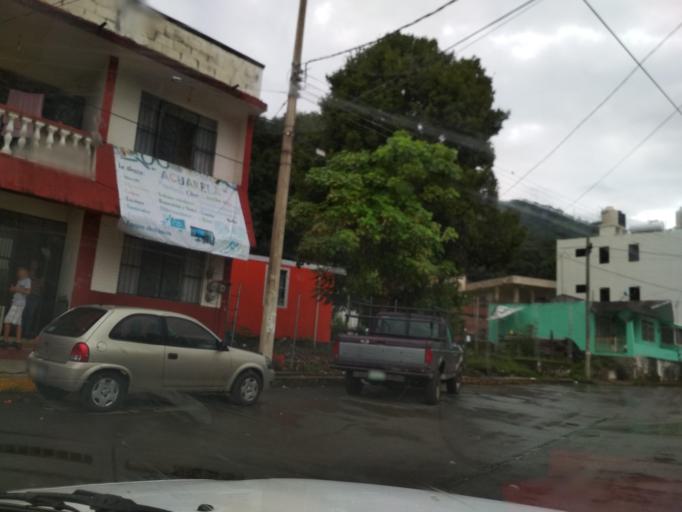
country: MX
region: Veracruz
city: San Andres Tuxtla
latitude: 18.4586
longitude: -95.2101
